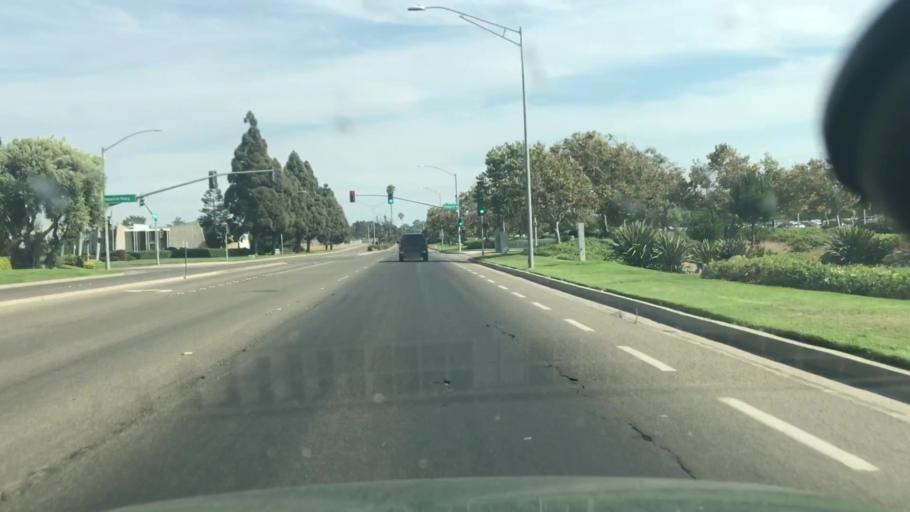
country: US
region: California
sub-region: Santa Barbara County
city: Orcutt
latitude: 34.9020
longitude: -120.4487
